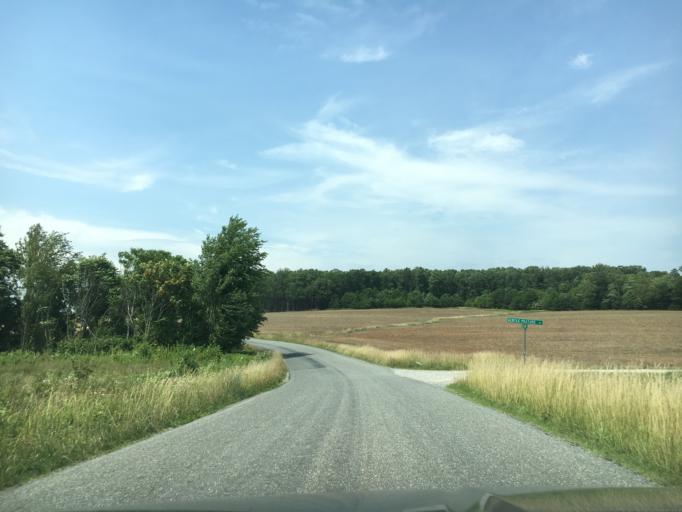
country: US
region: Virginia
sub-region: Pittsylvania County
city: Gretna
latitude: 36.9004
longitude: -79.4070
